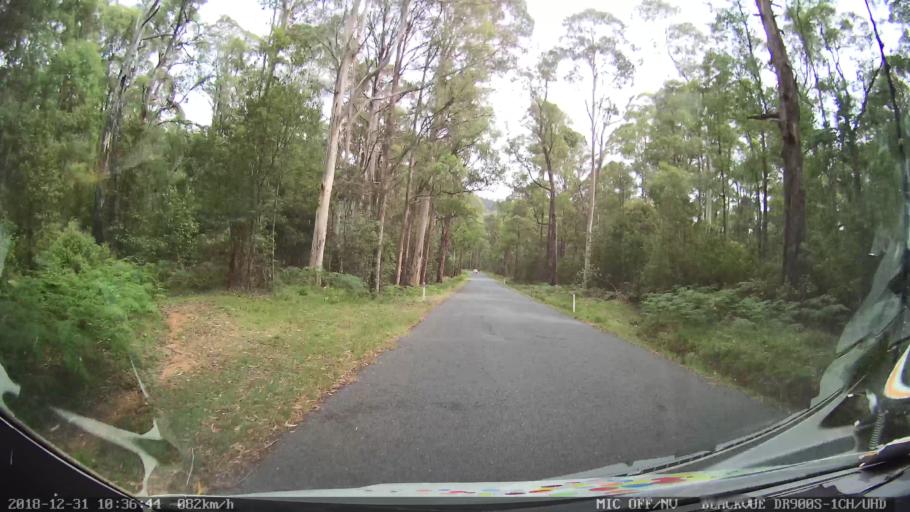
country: AU
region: New South Wales
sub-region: Snowy River
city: Jindabyne
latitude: -36.4231
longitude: 148.1710
